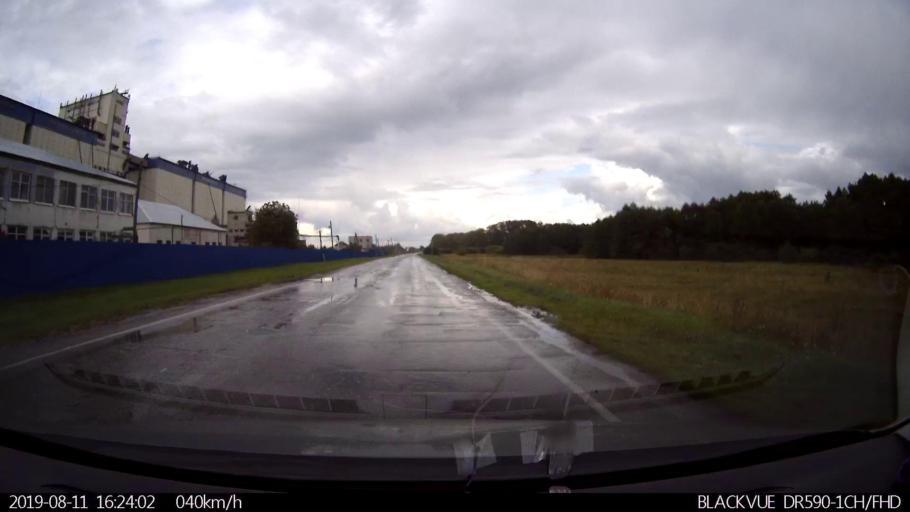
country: RU
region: Ulyanovsk
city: Mayna
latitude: 54.0983
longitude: 47.5909
